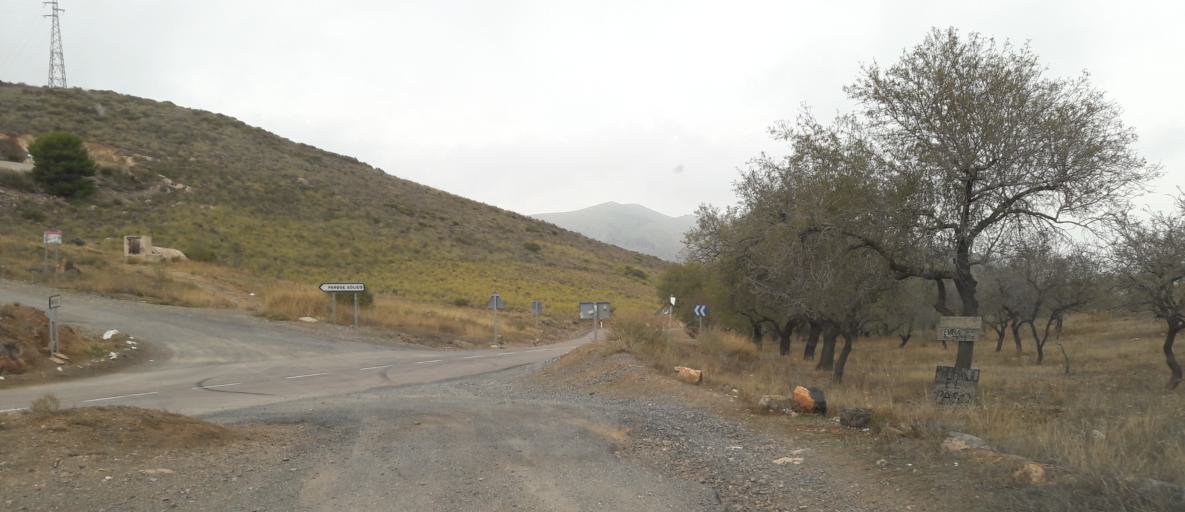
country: ES
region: Andalusia
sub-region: Provincia de Almeria
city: Enix
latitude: 36.8979
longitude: -2.6118
